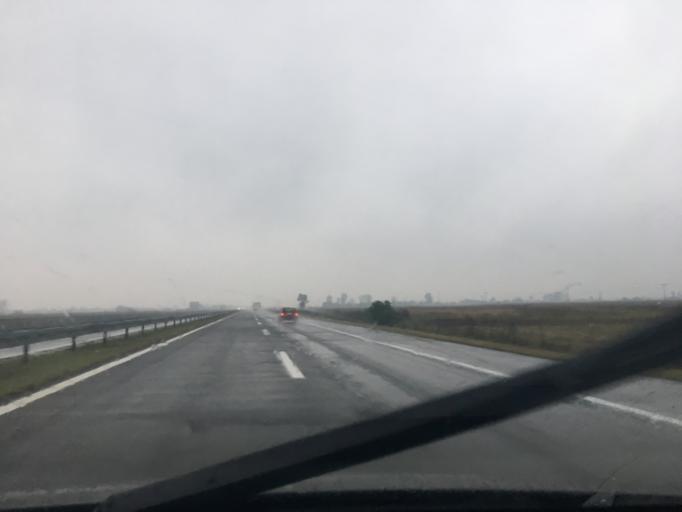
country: RS
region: Central Serbia
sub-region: Nisavski Okrug
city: Doljevac
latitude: 43.1236
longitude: 21.9131
